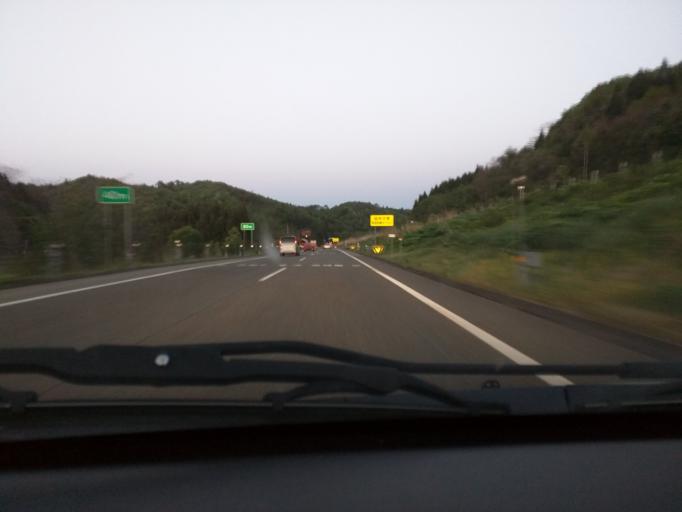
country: JP
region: Niigata
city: Kashiwazaki
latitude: 37.3392
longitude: 138.5315
